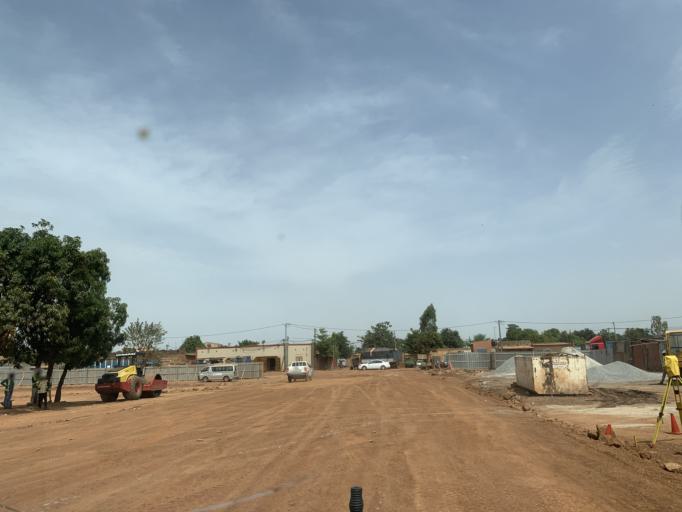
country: BF
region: Centre
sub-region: Kadiogo Province
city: Ouagadougou
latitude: 12.3346
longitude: -1.5162
